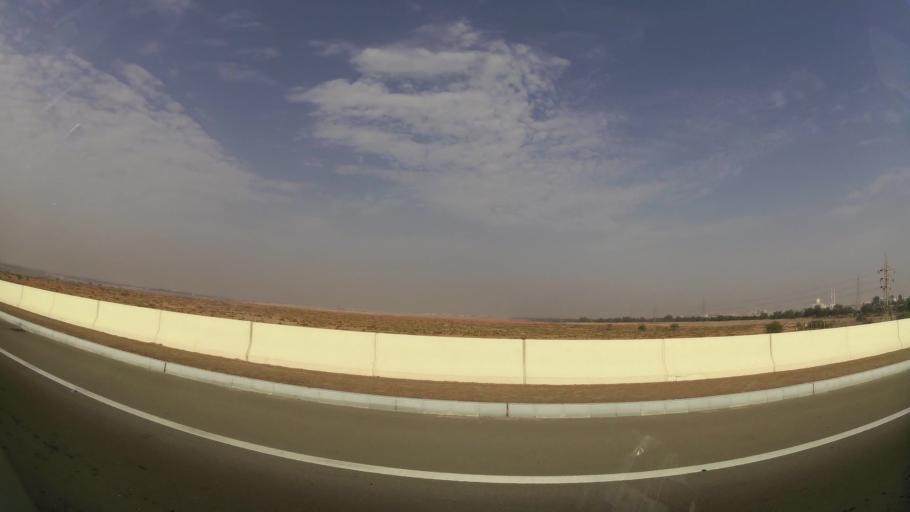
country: AE
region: Abu Dhabi
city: Abu Dhabi
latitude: 24.2485
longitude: 54.7063
